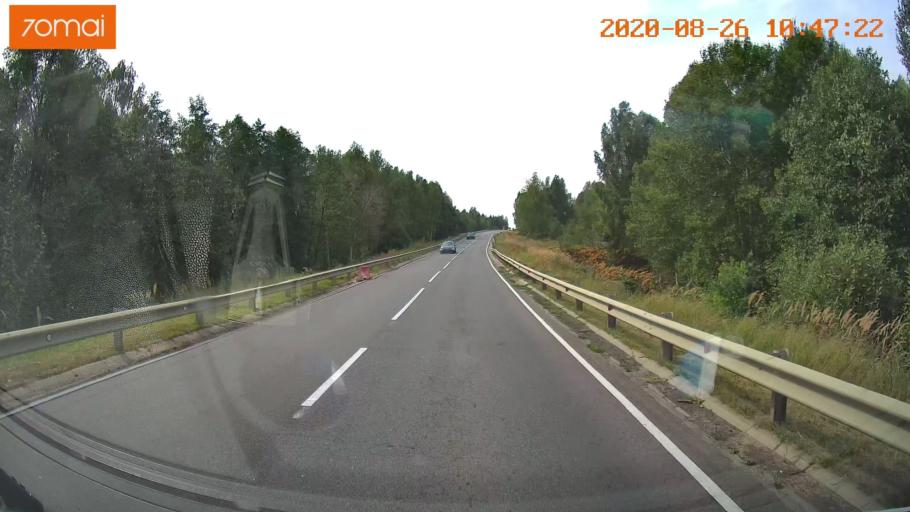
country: RU
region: Rjazan
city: Lashma
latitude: 54.7280
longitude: 41.1904
